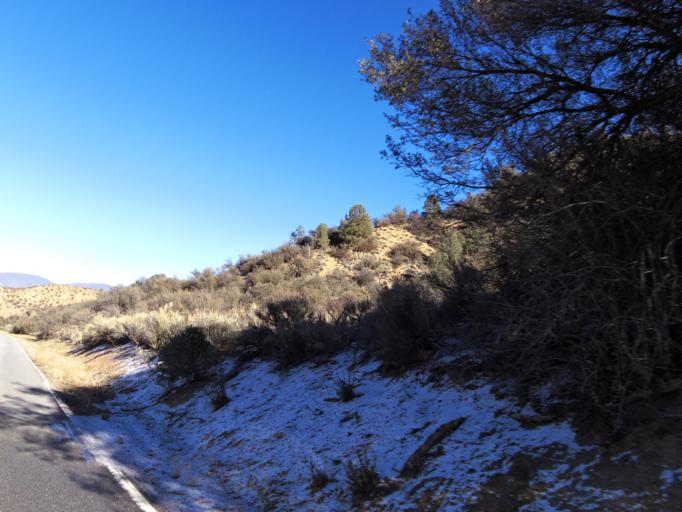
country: US
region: California
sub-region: Ventura County
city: Meiners Oaks
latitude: 34.6803
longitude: -119.3565
